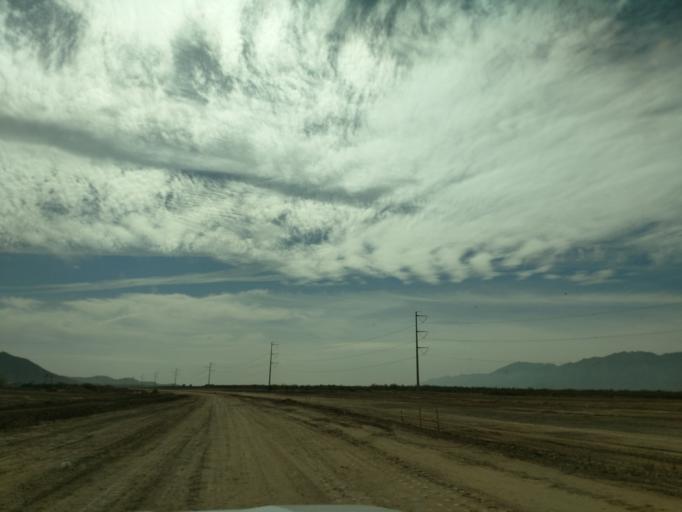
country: US
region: Arizona
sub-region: Maricopa County
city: Laveen
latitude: 33.3467
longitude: -112.1886
